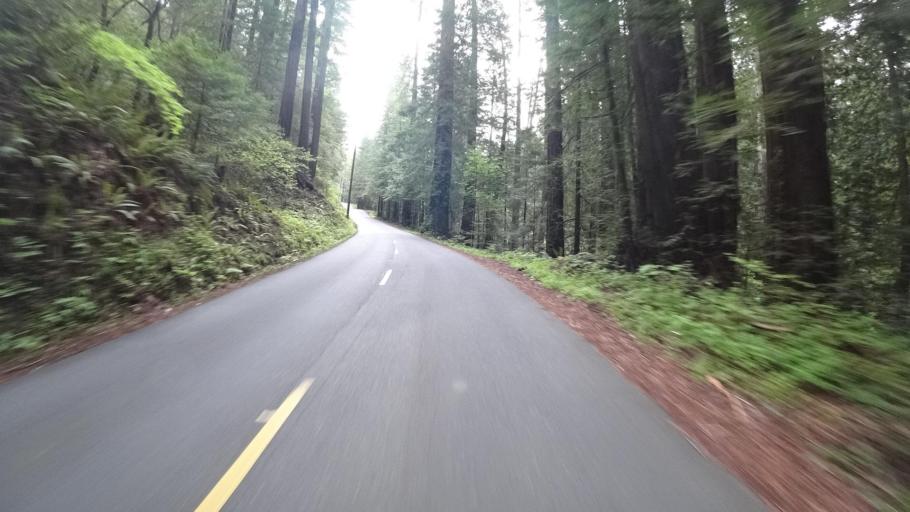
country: US
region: California
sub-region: Humboldt County
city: Redway
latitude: 40.2795
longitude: -123.8525
